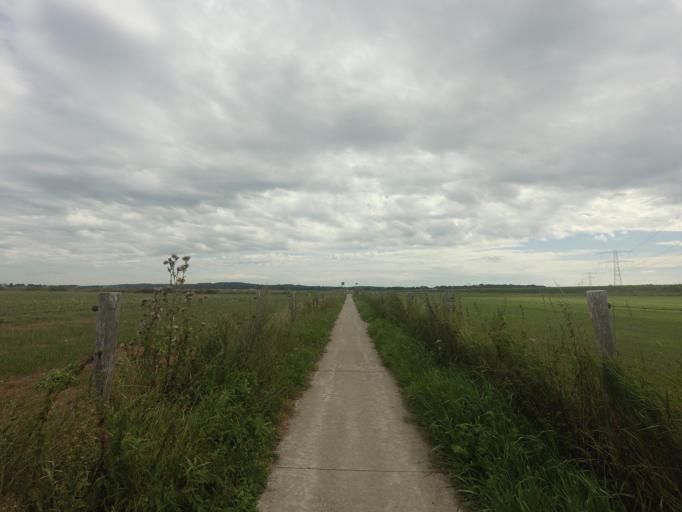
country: NL
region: Overijssel
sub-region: Gemeente Raalte
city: Raalte
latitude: 52.4538
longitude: 6.3588
